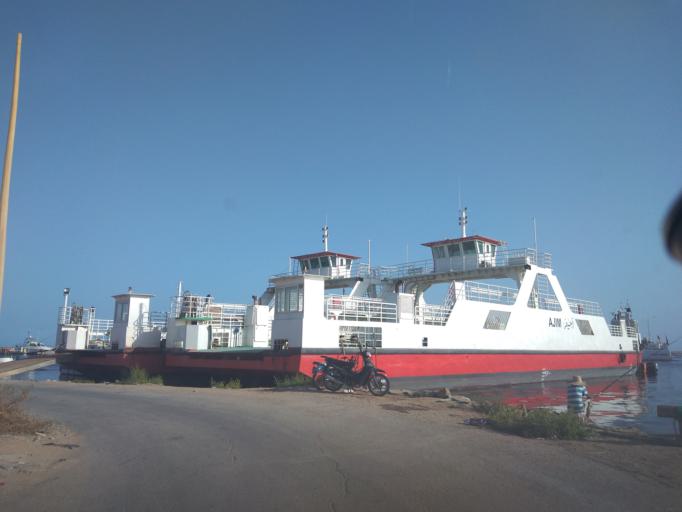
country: TN
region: Safaqis
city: Sfax
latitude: 34.7172
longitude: 10.7678
